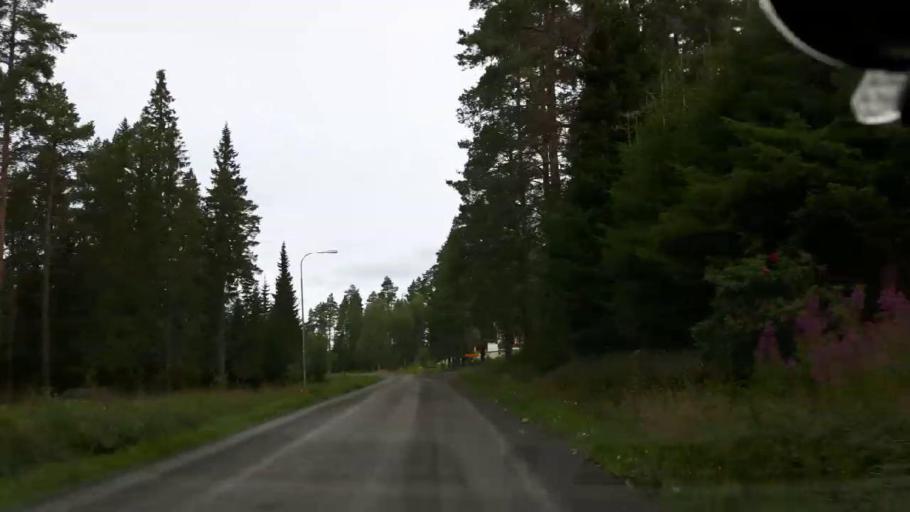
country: SE
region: Jaemtland
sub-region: Krokoms Kommun
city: Krokom
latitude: 63.3113
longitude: 14.3203
